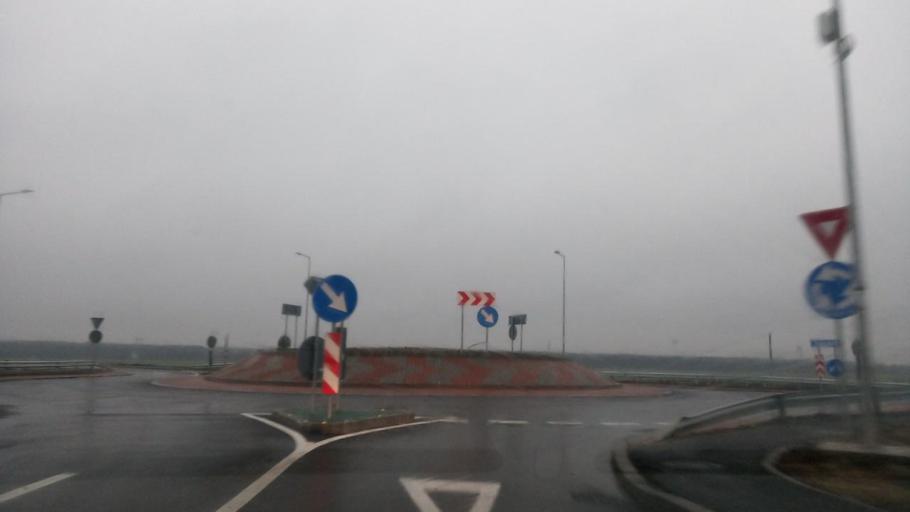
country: RO
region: Ilfov
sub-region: Comuna Branesti
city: Branesti
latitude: 44.4291
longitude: 26.3611
